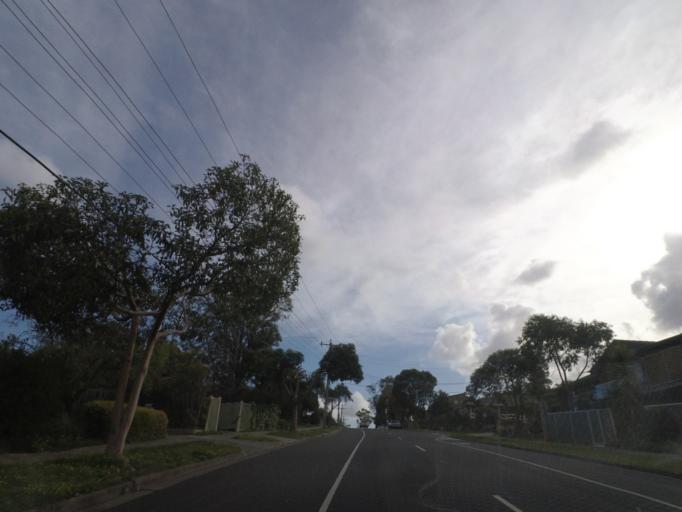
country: AU
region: Victoria
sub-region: Whitehorse
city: Vermont South
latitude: -37.8476
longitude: 145.1837
